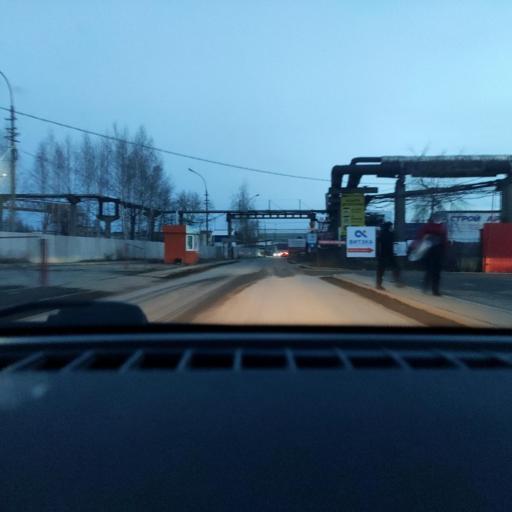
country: RU
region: Perm
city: Froly
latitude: 57.9649
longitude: 56.2714
